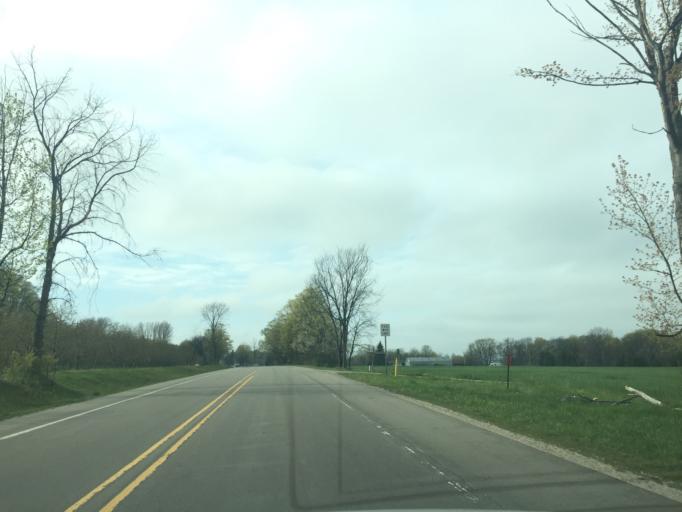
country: US
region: Michigan
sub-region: Leelanau County
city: Leland
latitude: 45.0724
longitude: -85.5883
